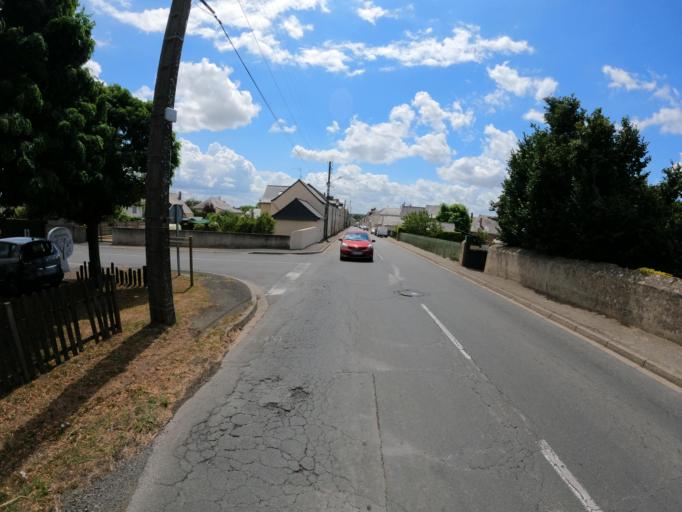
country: FR
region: Pays de la Loire
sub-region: Departement de Maine-et-Loire
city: Champigne
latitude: 47.6667
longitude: -0.5707
